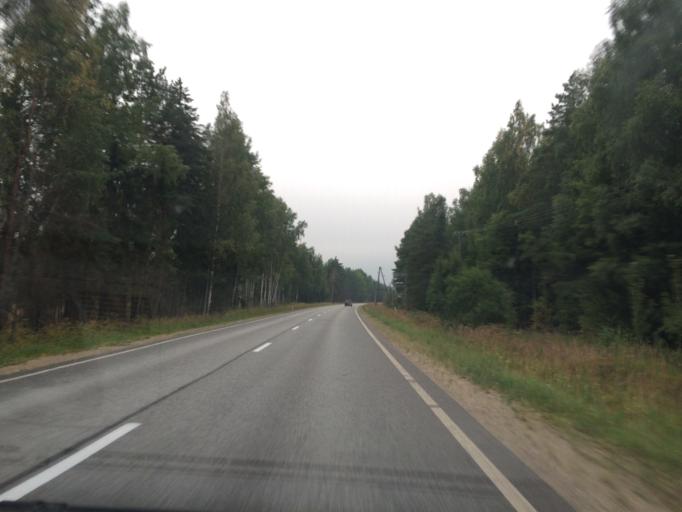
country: LV
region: Varaklani
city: Varaklani
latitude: 56.5348
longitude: 26.5501
